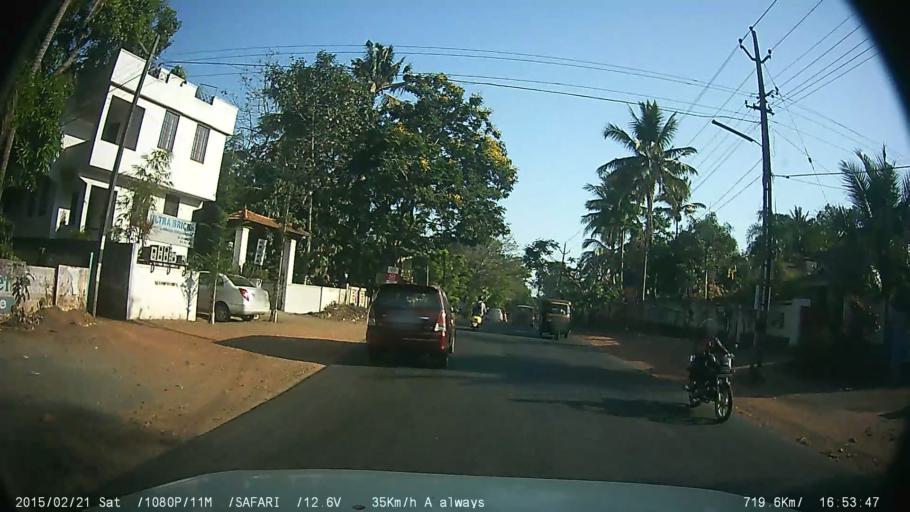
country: IN
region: Kerala
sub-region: Kottayam
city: Changanacheri
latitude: 9.4742
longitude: 76.5286
